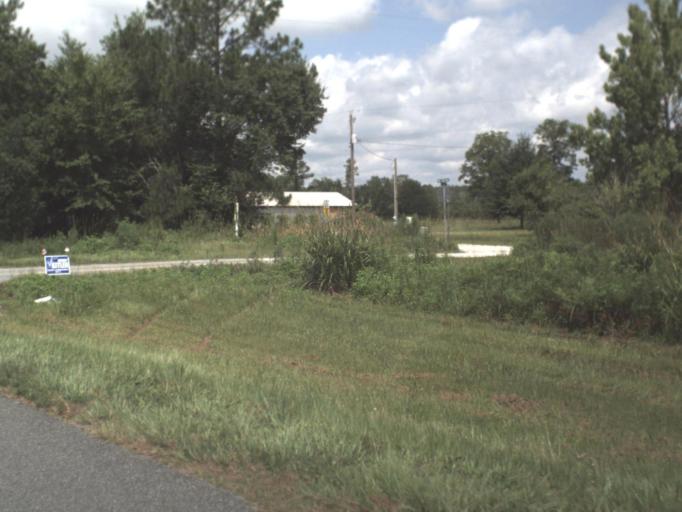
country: US
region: Florida
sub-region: Union County
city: Lake Butler
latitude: 30.0468
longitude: -82.2717
